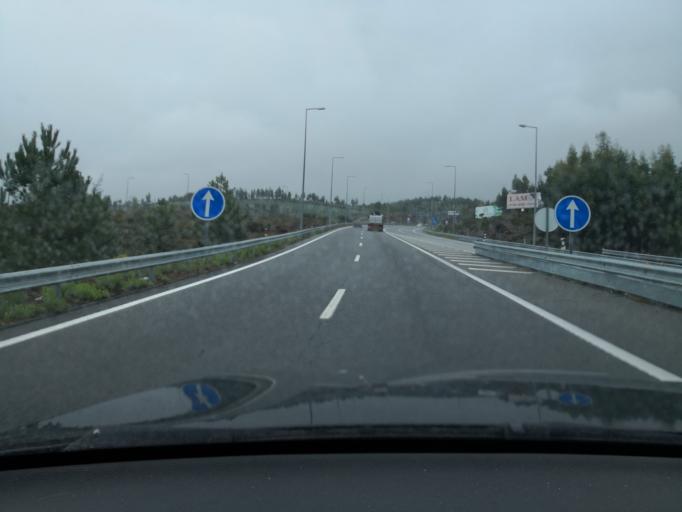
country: PT
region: Porto
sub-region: Valongo
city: Sobrado
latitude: 41.2311
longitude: -8.4538
